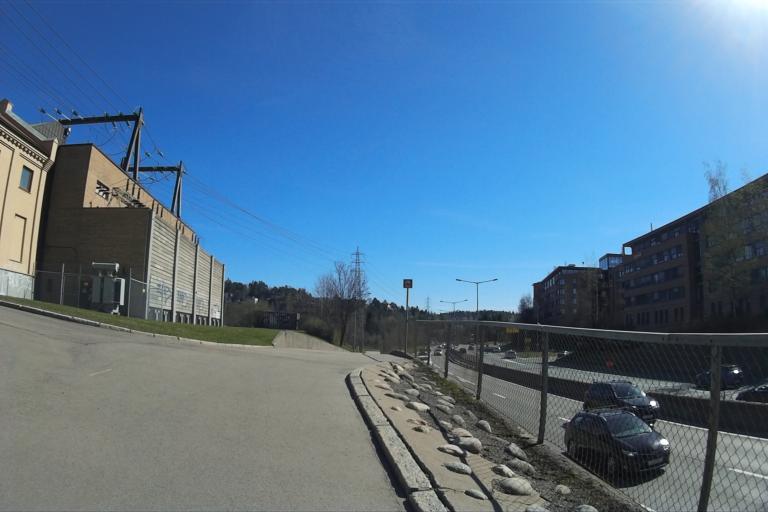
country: NO
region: Oslo
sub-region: Oslo
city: Oslo
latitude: 59.9125
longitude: 10.8174
